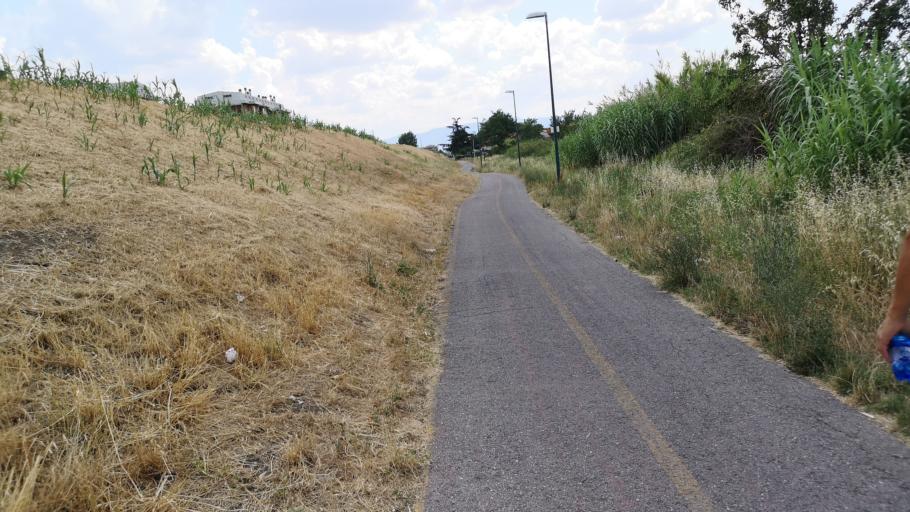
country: IT
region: Tuscany
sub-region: Provincia di Prato
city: Fornacelle
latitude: 43.8993
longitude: 11.0636
